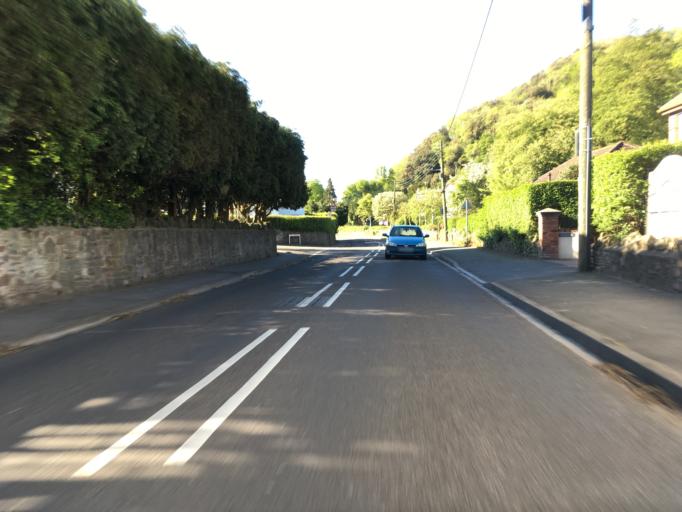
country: GB
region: England
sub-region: North Somerset
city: Clevedon
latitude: 51.4438
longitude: -2.8418
